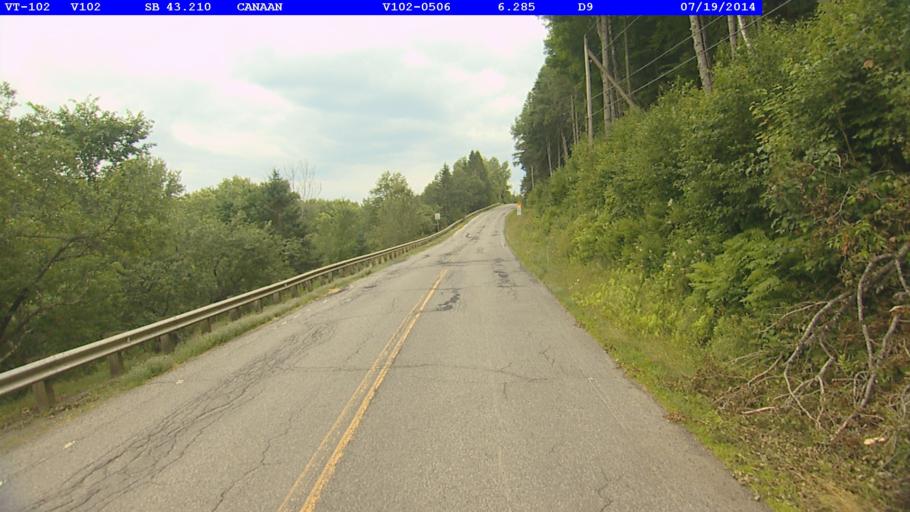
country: US
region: New Hampshire
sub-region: Coos County
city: Colebrook
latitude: 44.9892
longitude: -71.5423
